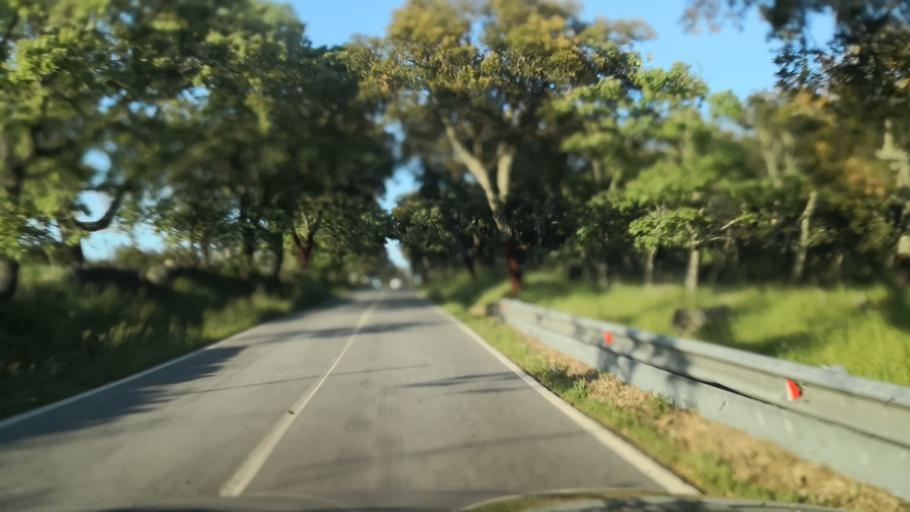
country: PT
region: Portalegre
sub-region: Portalegre
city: Portalegre
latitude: 39.3362
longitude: -7.4193
